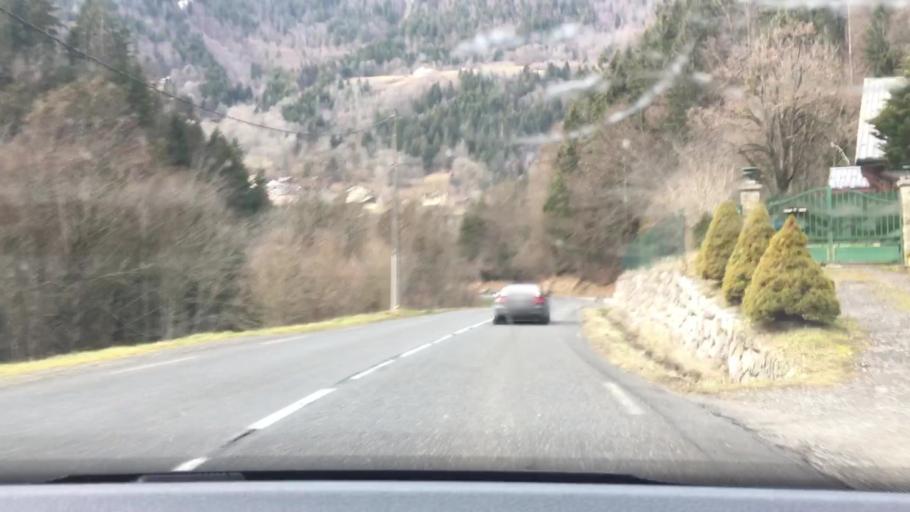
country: FR
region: Rhone-Alpes
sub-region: Departement de la Haute-Savoie
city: Abondance
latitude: 46.2960
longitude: 6.6786
